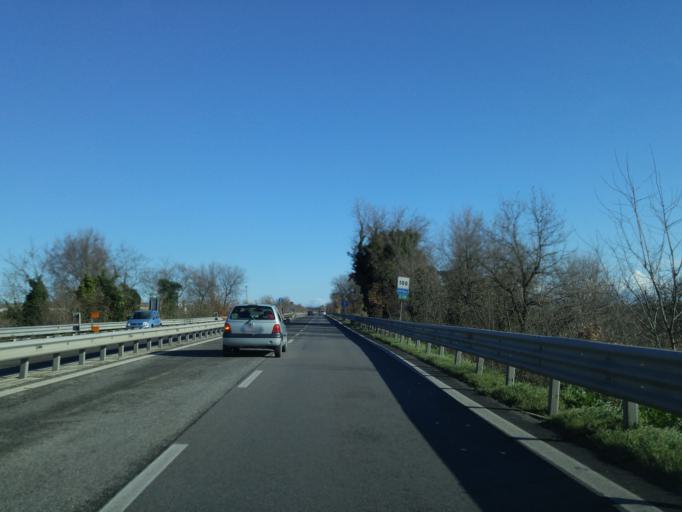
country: IT
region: The Marches
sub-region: Provincia di Pesaro e Urbino
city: Calcinelli
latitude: 43.7558
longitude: 12.9317
